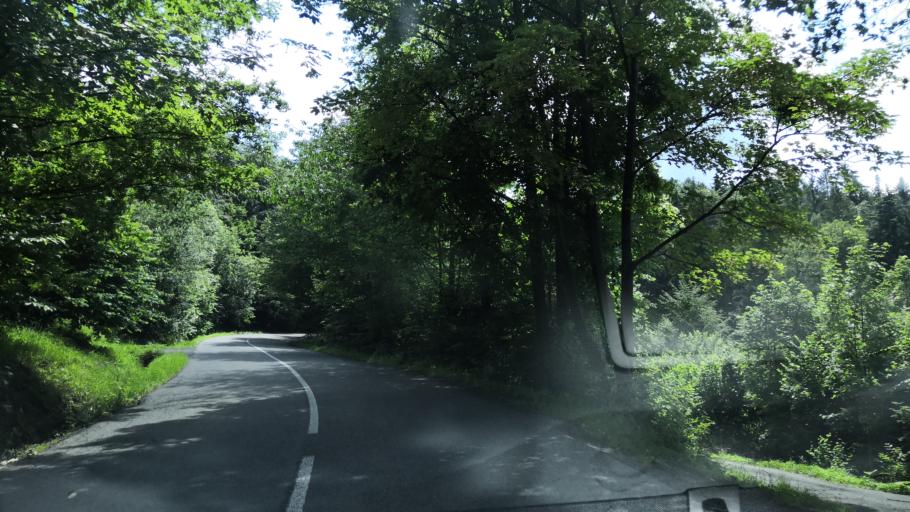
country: CZ
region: Zlin
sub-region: Okres Vsetin
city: Roznov pod Radhostem
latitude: 49.4335
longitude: 18.1316
